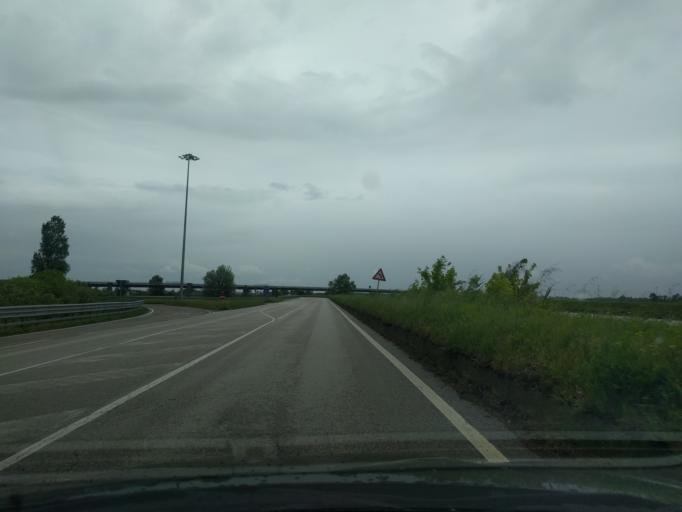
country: IT
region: Veneto
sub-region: Provincia di Rovigo
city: Bottrighe
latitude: 45.0486
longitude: 12.0956
